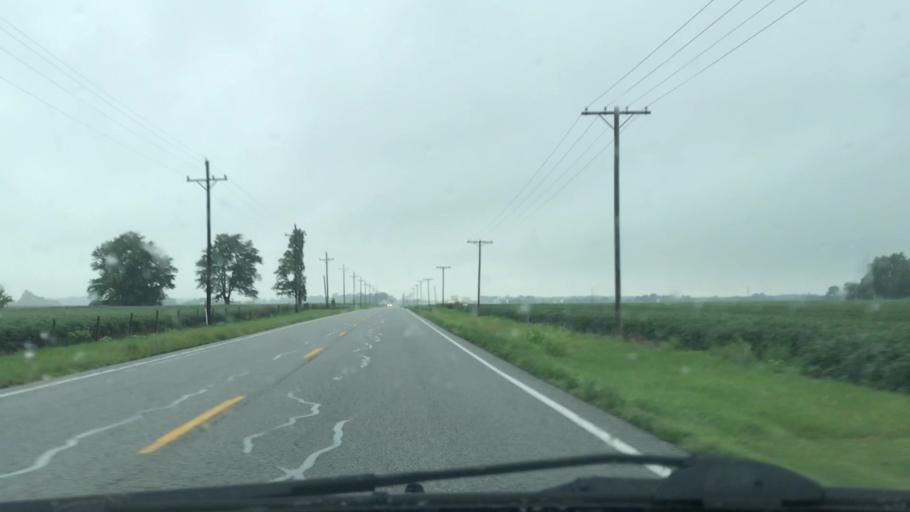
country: US
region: Indiana
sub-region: Hamilton County
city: Sheridan
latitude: 40.1283
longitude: -86.3130
